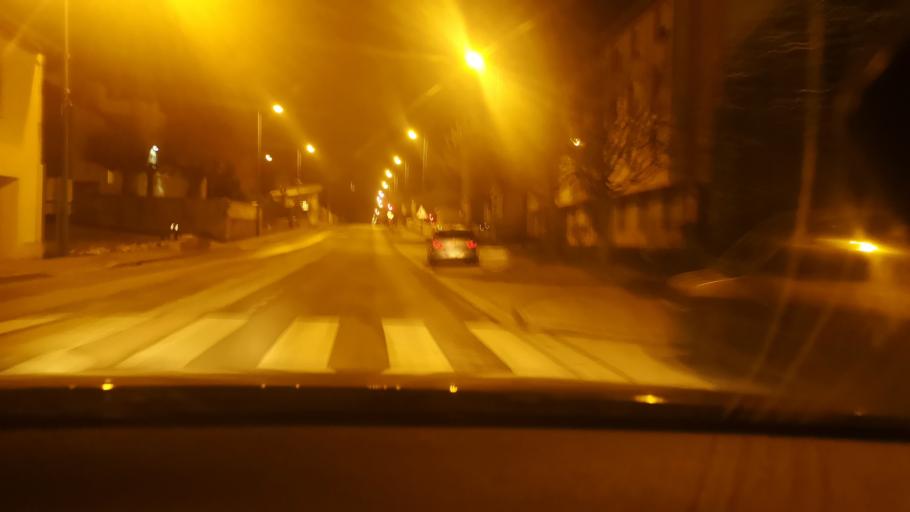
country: FR
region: Rhone-Alpes
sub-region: Departement de l'Ain
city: Montrevel-en-Bresse
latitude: 46.3395
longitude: 5.1278
